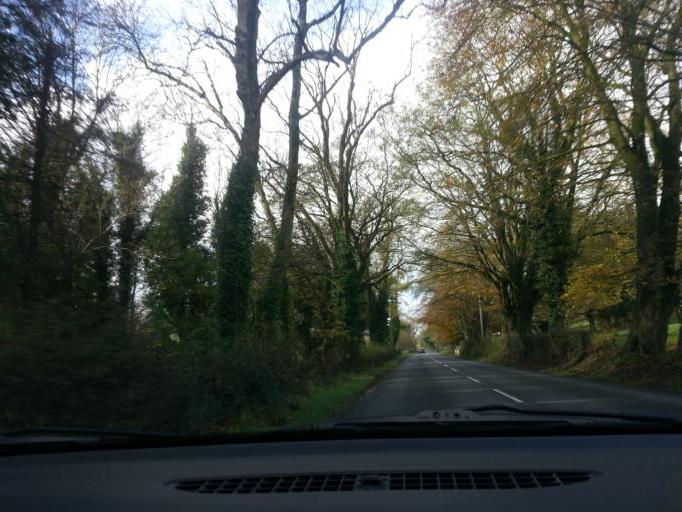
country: GB
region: Northern Ireland
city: Lisnaskea
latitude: 54.2183
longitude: -7.4048
